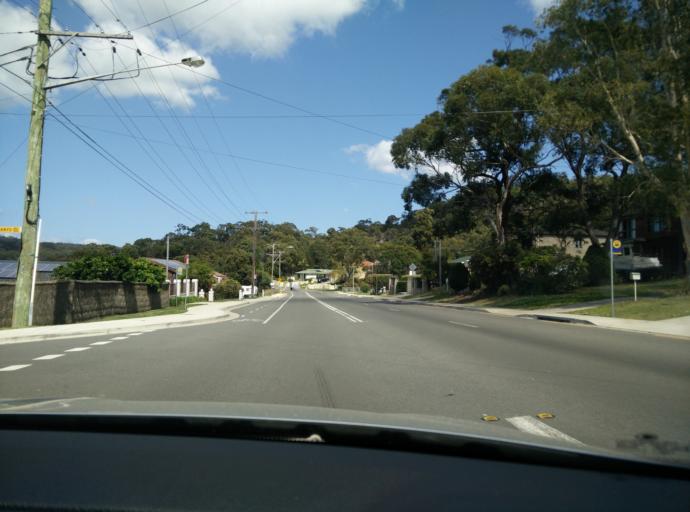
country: AU
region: New South Wales
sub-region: Gosford Shire
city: Blackwall
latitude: -33.4892
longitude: 151.3012
